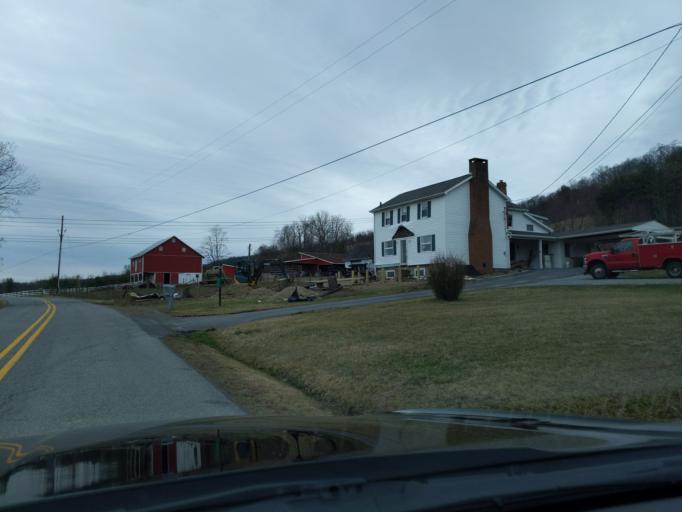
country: US
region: Pennsylvania
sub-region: Blair County
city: Greenwood
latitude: 40.5866
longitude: -78.3771
